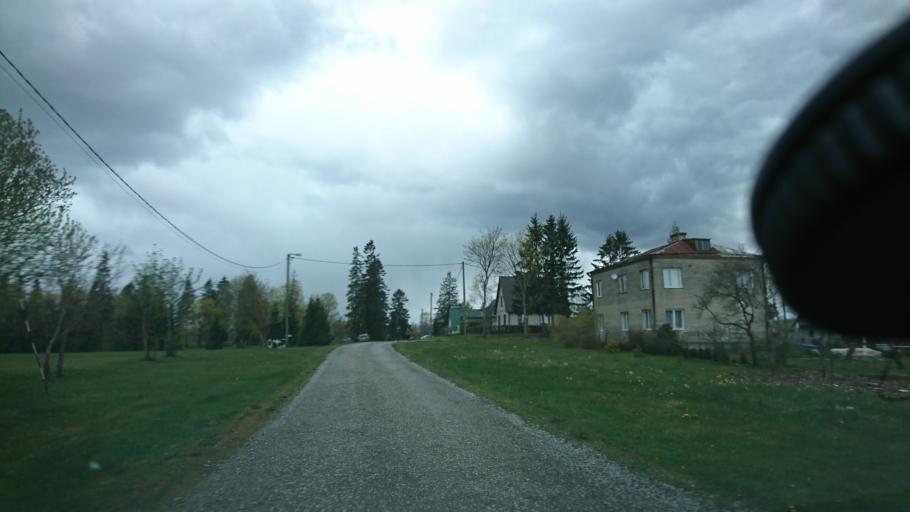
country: EE
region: Laeaene-Virumaa
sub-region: Tapa vald
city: Tapa
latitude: 59.2573
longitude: 25.9660
